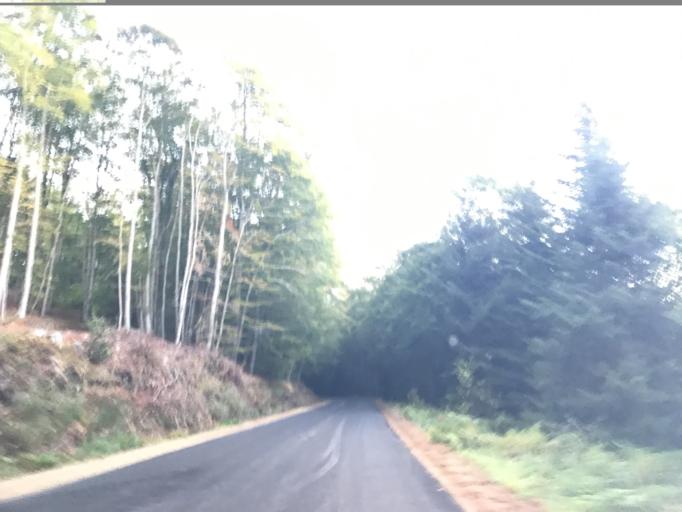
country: FR
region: Auvergne
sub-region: Departement du Puy-de-Dome
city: Celles-sur-Durolle
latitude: 45.8103
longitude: 3.6619
